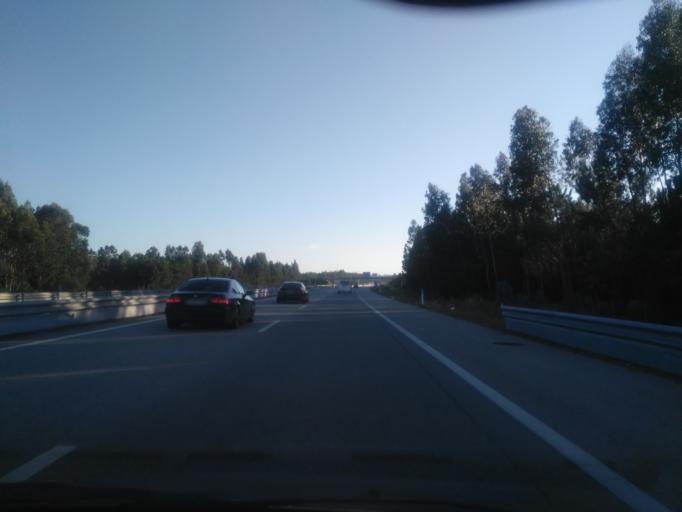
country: PT
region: Coimbra
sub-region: Figueira da Foz
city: Alhadas
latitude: 40.2273
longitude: -8.7916
